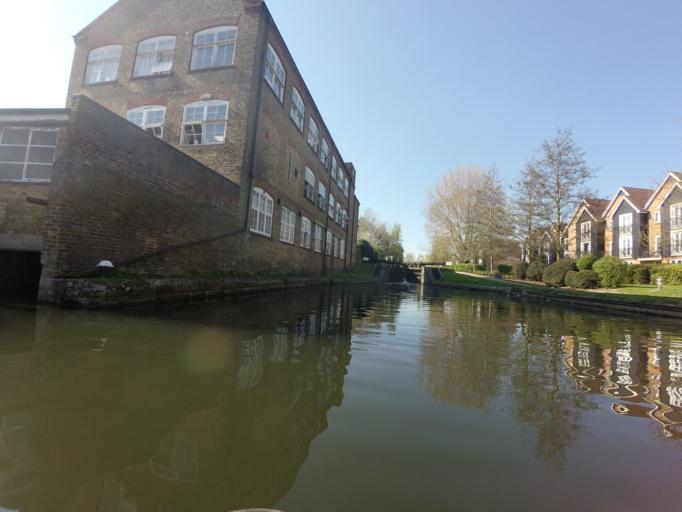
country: GB
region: England
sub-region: Hertfordshire
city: Kings Langley
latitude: 51.7338
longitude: -0.4614
